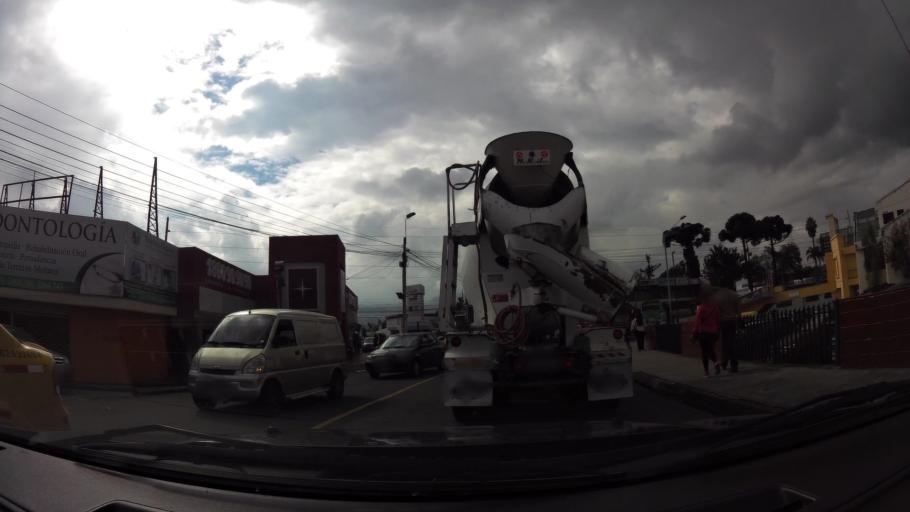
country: EC
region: Pichincha
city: Sangolqui
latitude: -0.3006
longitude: -78.4602
